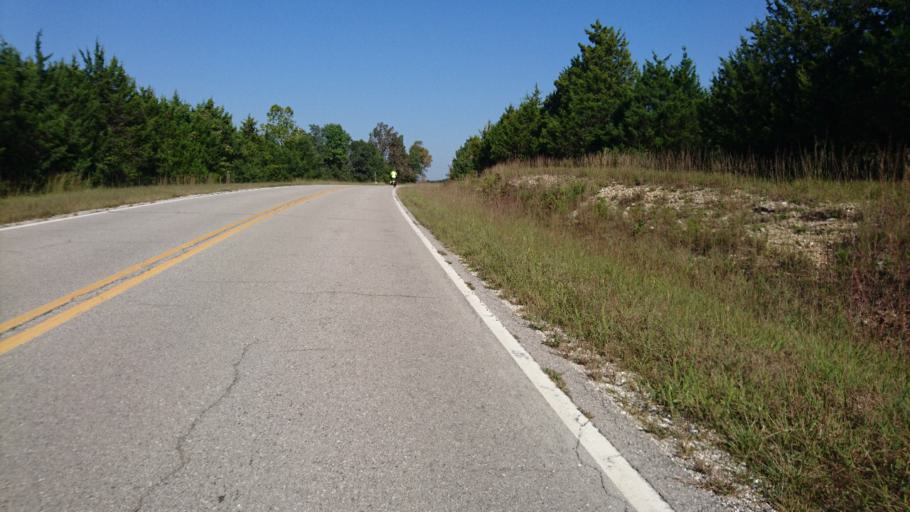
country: US
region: Missouri
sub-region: Pulaski County
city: Richland
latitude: 37.7537
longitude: -92.3728
